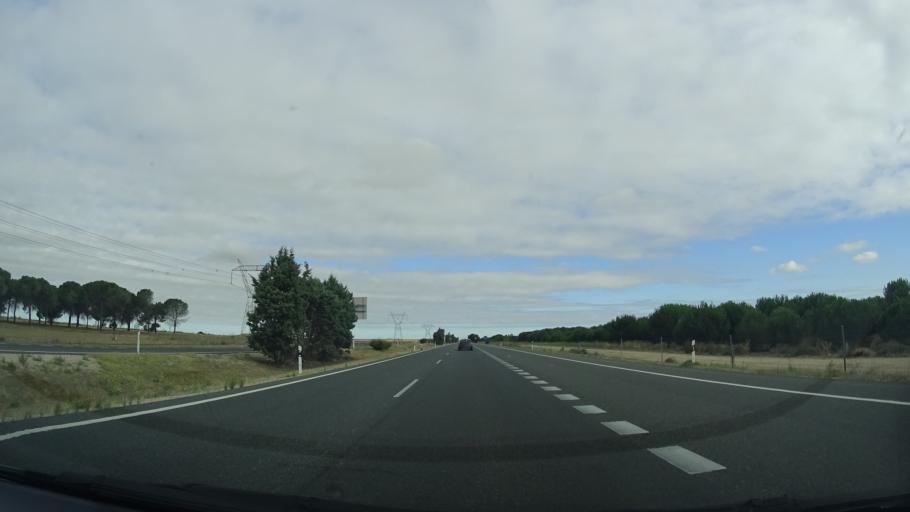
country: ES
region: Castille and Leon
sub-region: Provincia de Valladolid
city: San Pablo de la Moraleja
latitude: 41.1518
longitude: -4.7907
